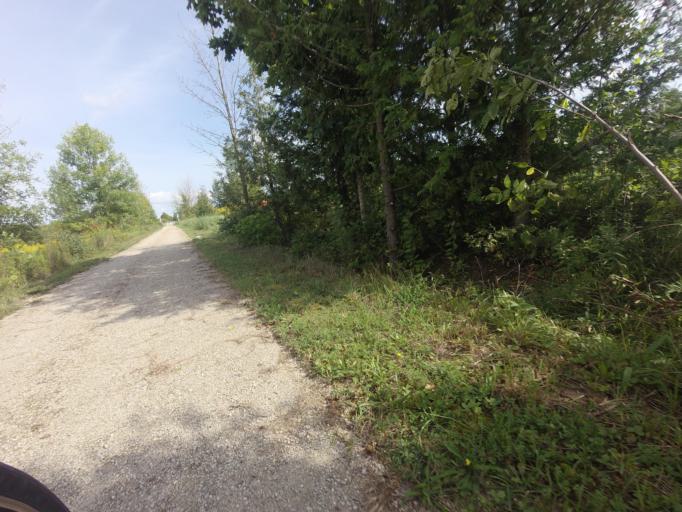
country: CA
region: Ontario
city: Waterloo
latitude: 43.5885
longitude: -80.4424
